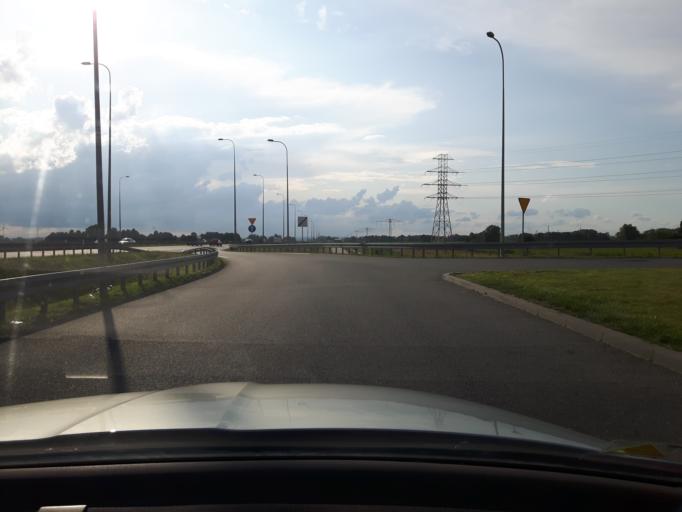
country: PL
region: Pomeranian Voivodeship
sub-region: Powiat gdanski
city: Cedry Wielkie
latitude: 54.3052
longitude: 18.7935
